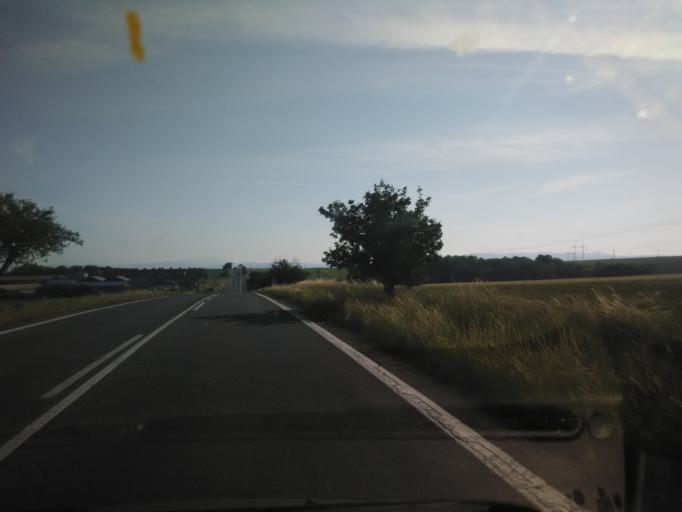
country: SK
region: Nitriansky
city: Levice
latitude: 48.2455
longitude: 18.6813
